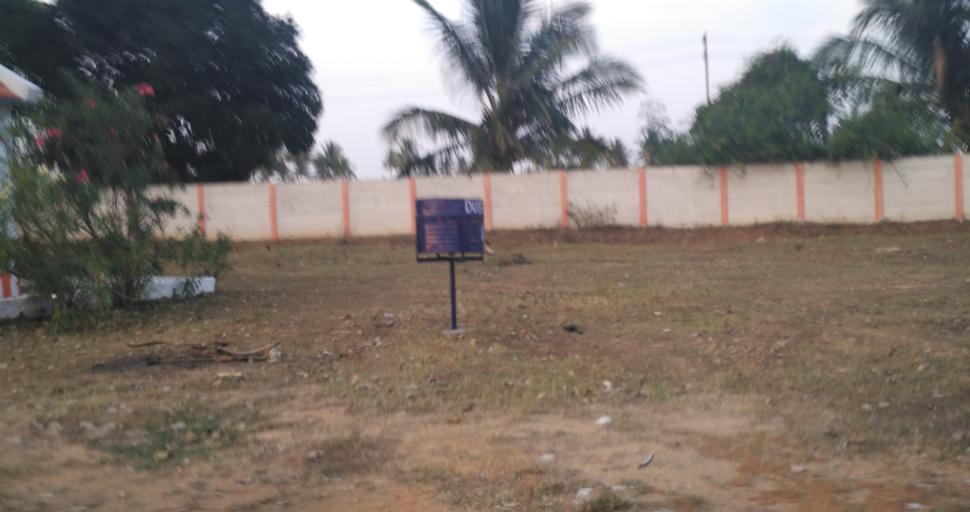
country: IN
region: Tamil Nadu
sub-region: Krishnagiri
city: Hosur
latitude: 12.6713
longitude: 77.8265
